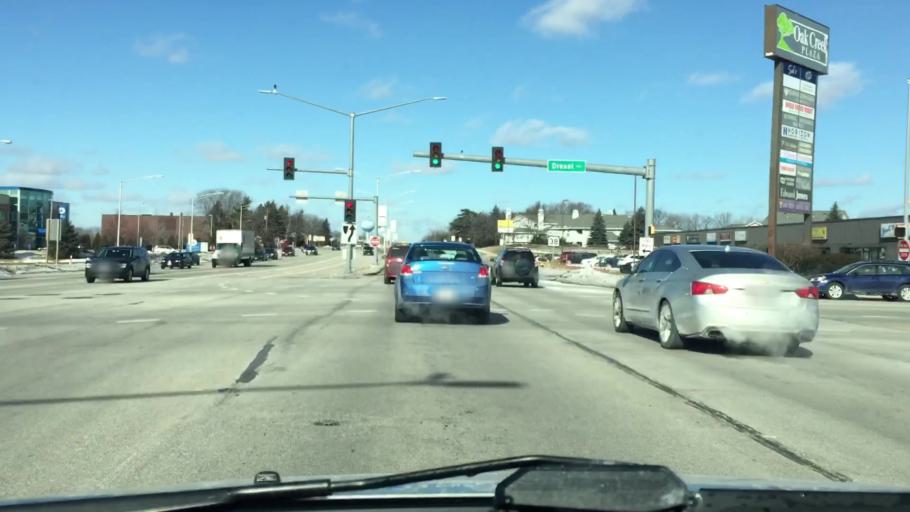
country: US
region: Wisconsin
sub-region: Milwaukee County
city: Oak Creek
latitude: 42.9010
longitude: -87.9115
